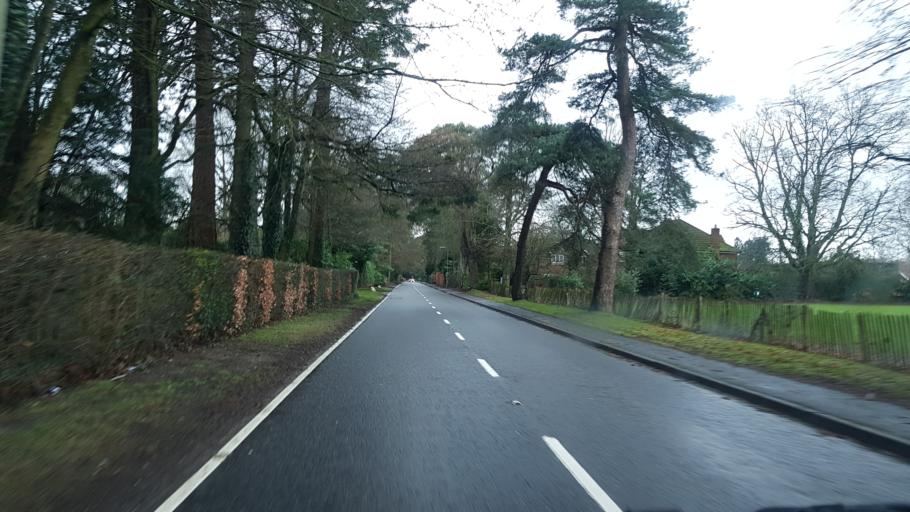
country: GB
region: England
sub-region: Surrey
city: Churt
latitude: 51.1111
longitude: -0.7640
